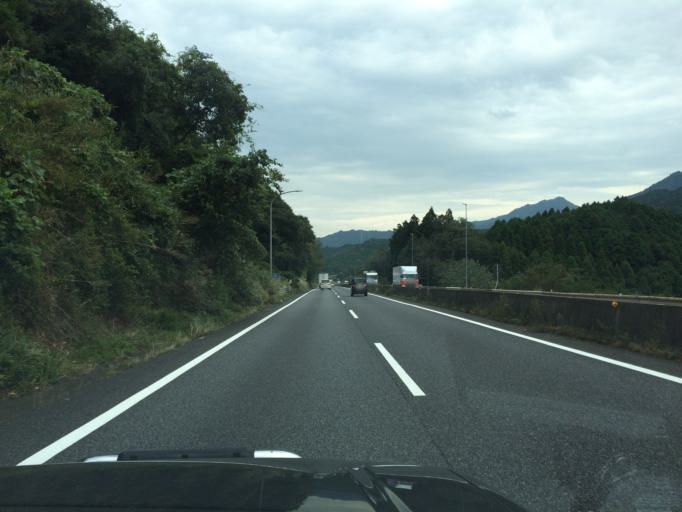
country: JP
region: Mie
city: Kameyama
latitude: 34.8354
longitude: 136.2997
